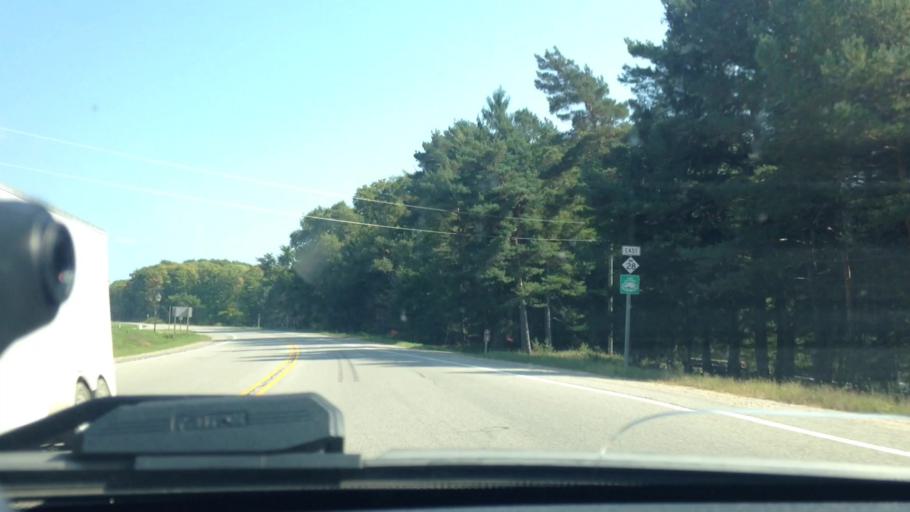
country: US
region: Michigan
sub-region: Luce County
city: Newberry
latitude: 46.3106
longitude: -85.6568
